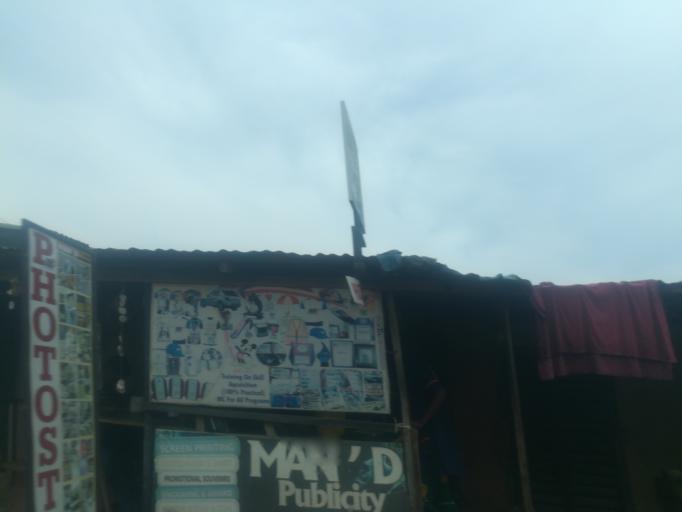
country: NG
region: Oyo
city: Ibadan
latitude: 7.3741
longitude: 3.9312
